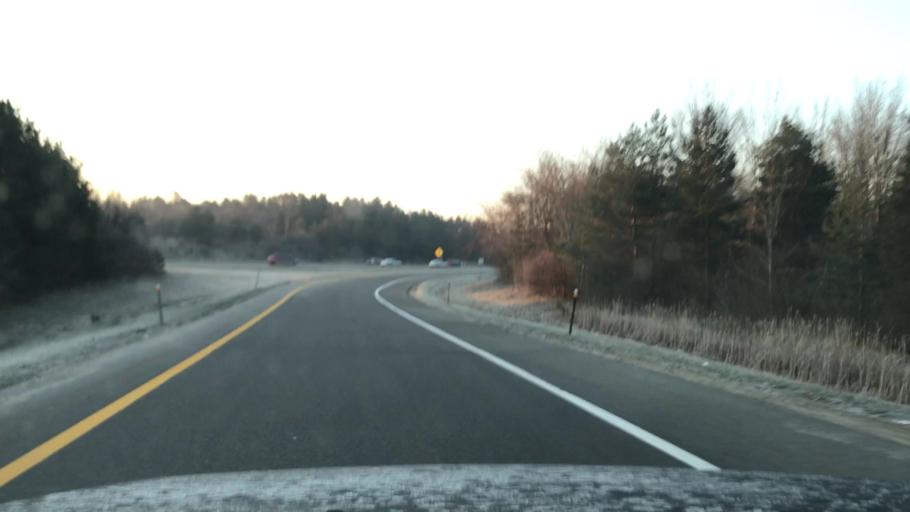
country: US
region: Michigan
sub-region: Kent County
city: East Grand Rapids
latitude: 42.9835
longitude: -85.6065
